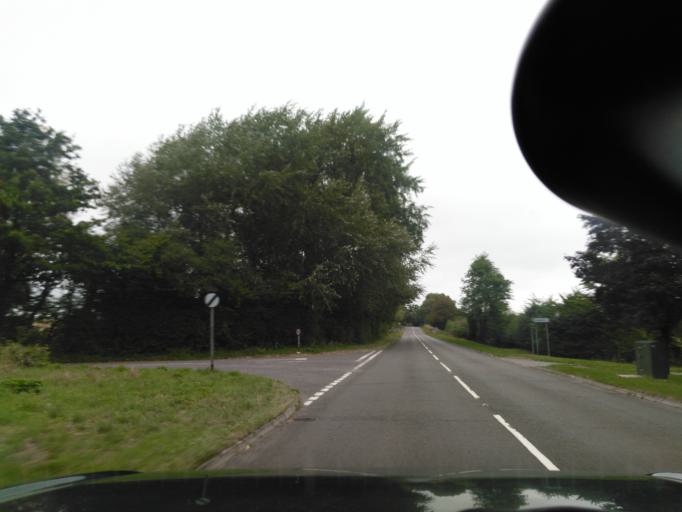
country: GB
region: England
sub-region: Dorset
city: Shaftesbury
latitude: 51.0486
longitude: -2.1836
